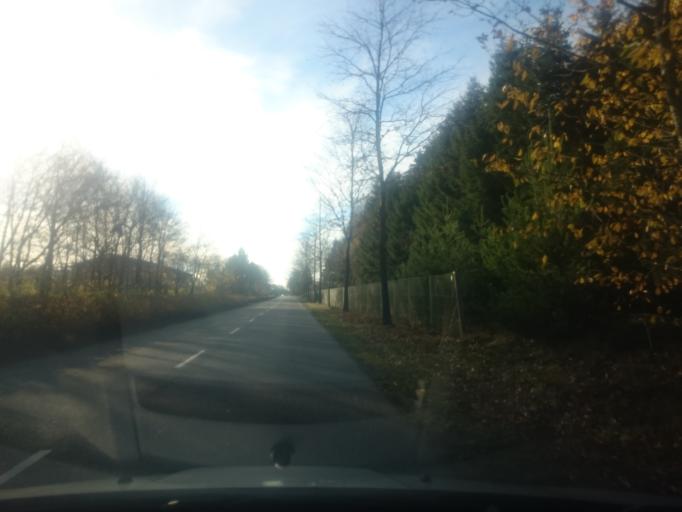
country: DK
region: South Denmark
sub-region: Billund Kommune
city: Billund
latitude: 55.7382
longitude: 9.1128
